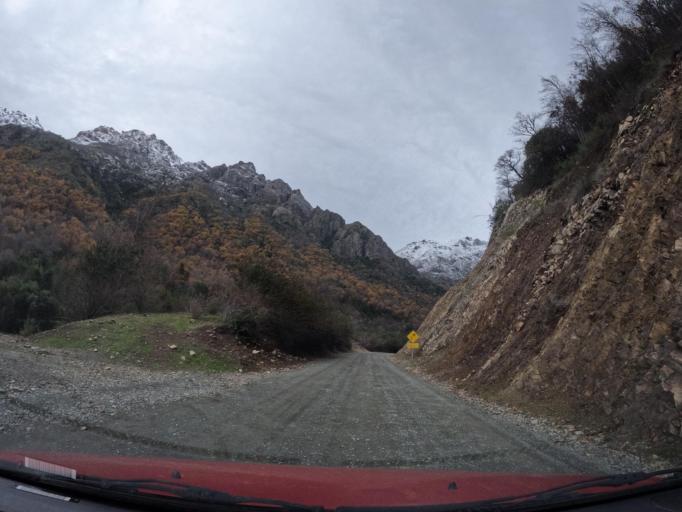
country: CL
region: Maule
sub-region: Provincia de Linares
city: Colbun
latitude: -35.8622
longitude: -71.1253
